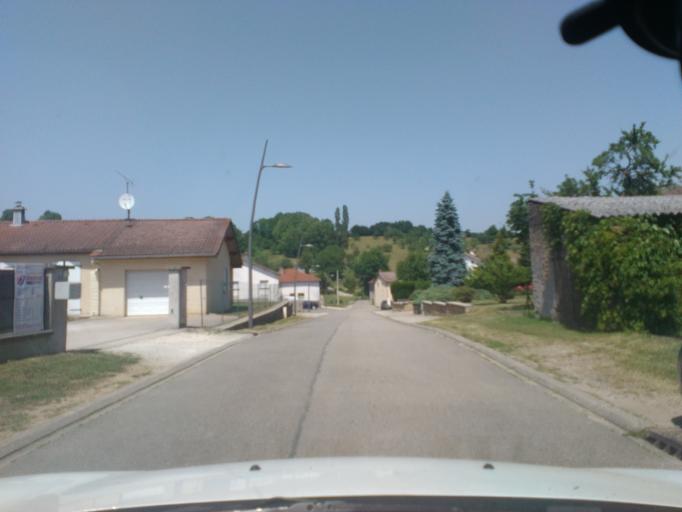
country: FR
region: Lorraine
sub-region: Departement des Vosges
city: Mirecourt
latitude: 48.3105
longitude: 6.0994
